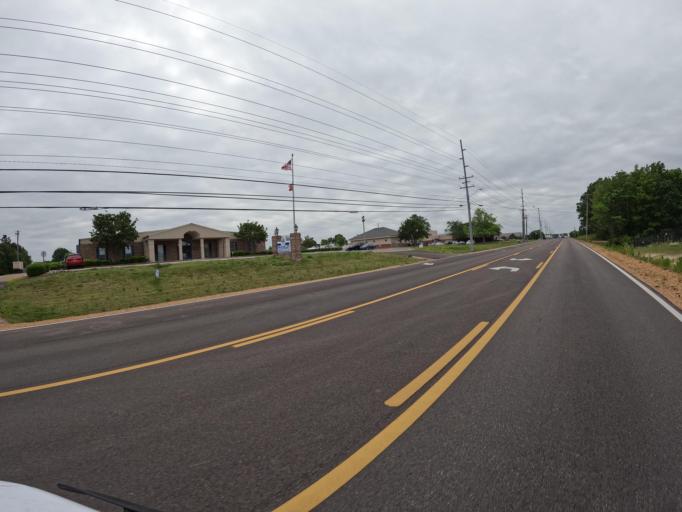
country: US
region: Mississippi
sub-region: Lee County
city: Tupelo
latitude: 34.2697
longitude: -88.7643
